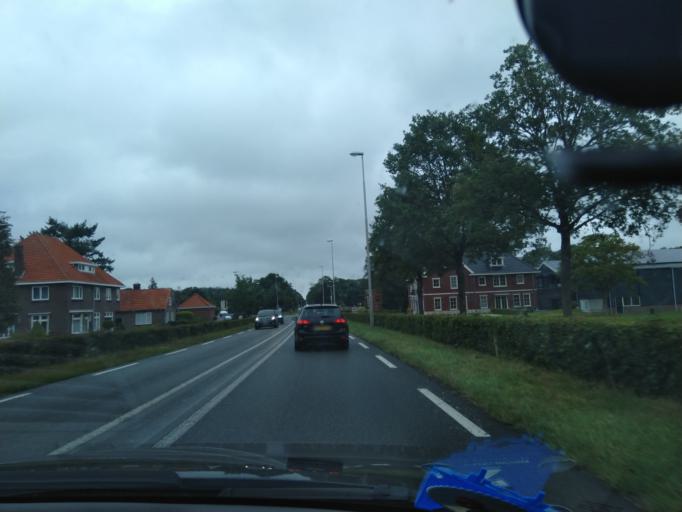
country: NL
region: Overijssel
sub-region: Gemeente Oldenzaal
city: Oldenzaal
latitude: 52.3592
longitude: 6.9863
